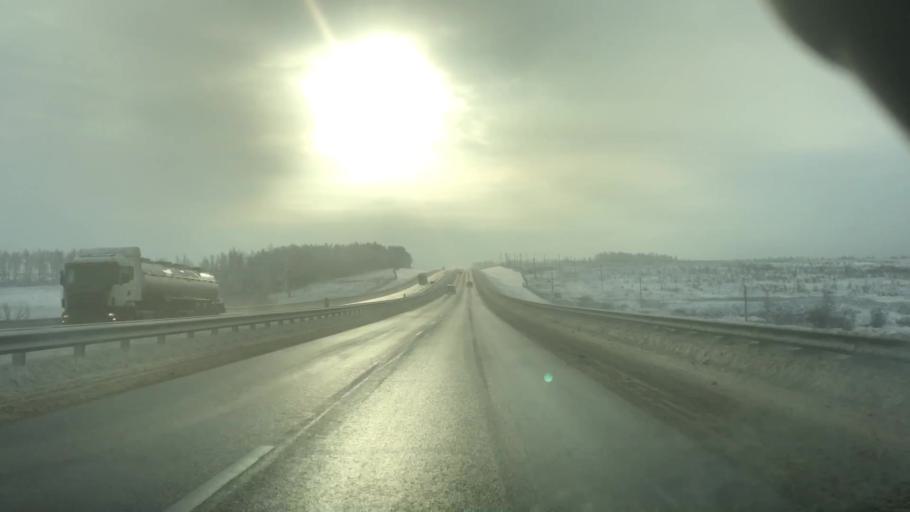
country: RU
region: Tula
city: Venev
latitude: 54.3203
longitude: 38.1544
